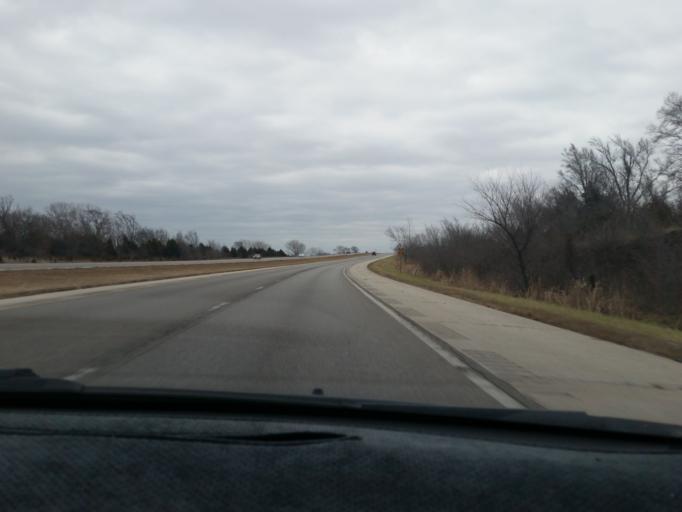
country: US
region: Kansas
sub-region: Johnson County
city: De Soto
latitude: 38.9615
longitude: -95.0122
